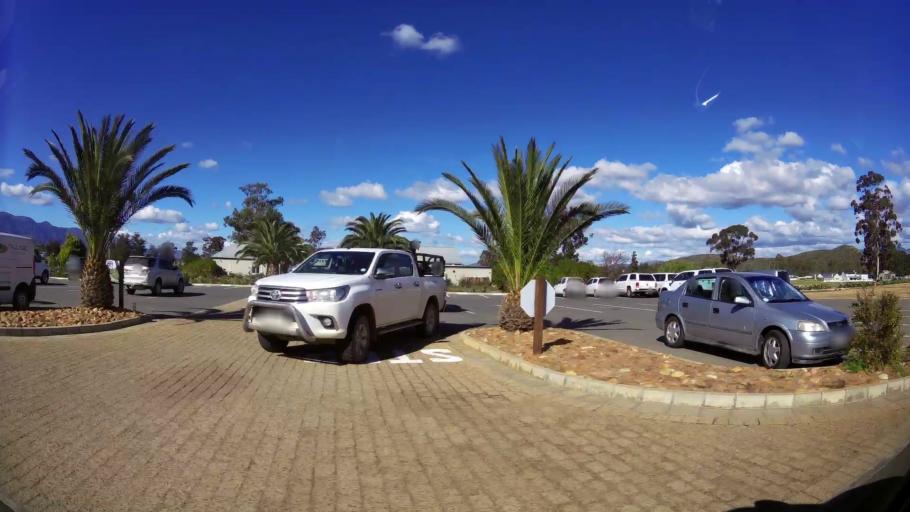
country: ZA
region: Western Cape
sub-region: Cape Winelands District Municipality
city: Ashton
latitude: -33.8103
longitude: 19.8509
